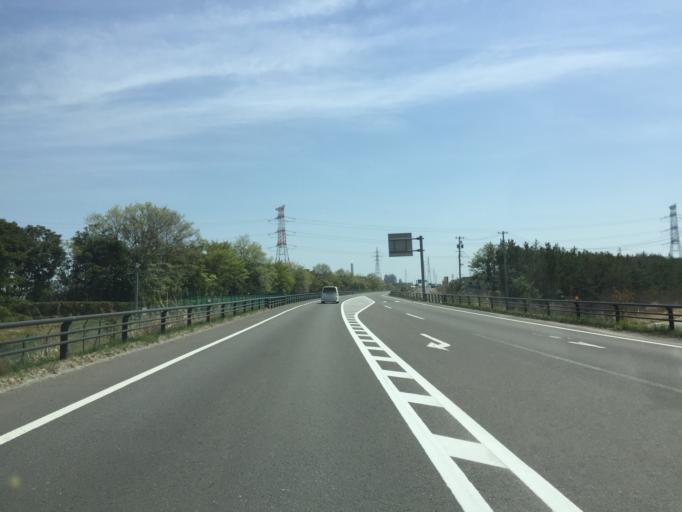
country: JP
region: Miyagi
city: Marumori
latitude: 37.8446
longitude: 140.9356
